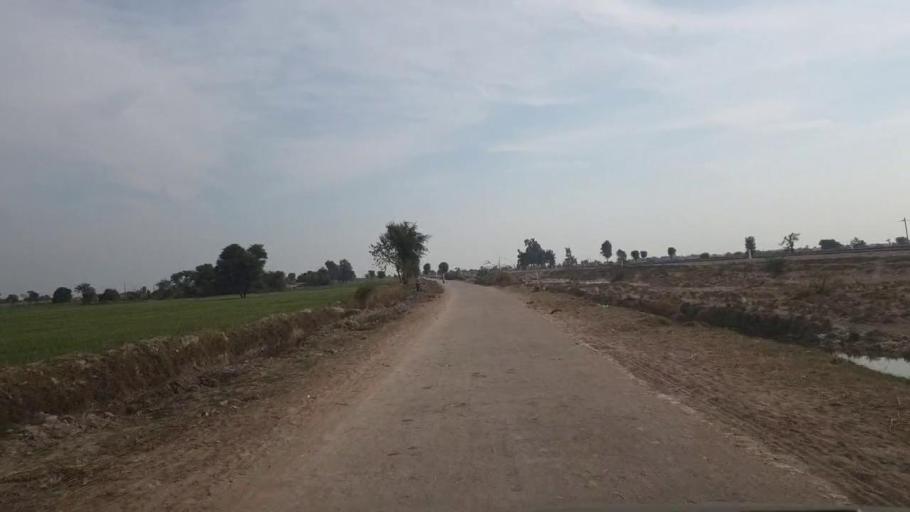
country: PK
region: Sindh
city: Nawabshah
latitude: 26.0902
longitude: 68.4841
